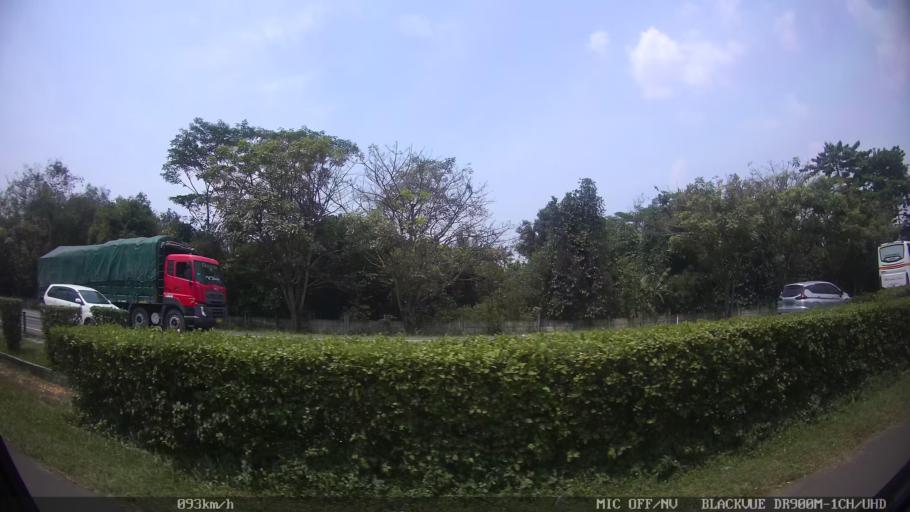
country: ID
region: Banten
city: Serang
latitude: -6.0737
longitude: 106.1298
